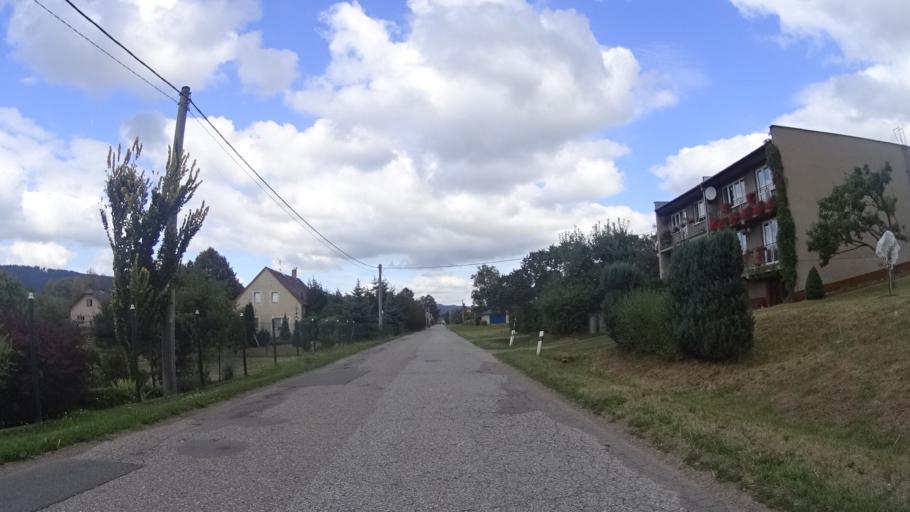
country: CZ
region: Pardubicky
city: Dolni Cermna
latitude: 49.9246
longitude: 16.5505
